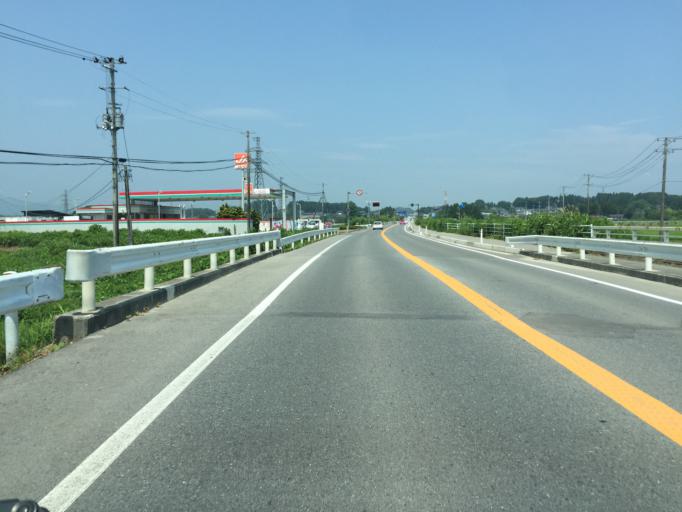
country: JP
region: Miyagi
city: Marumori
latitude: 37.8278
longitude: 140.9188
